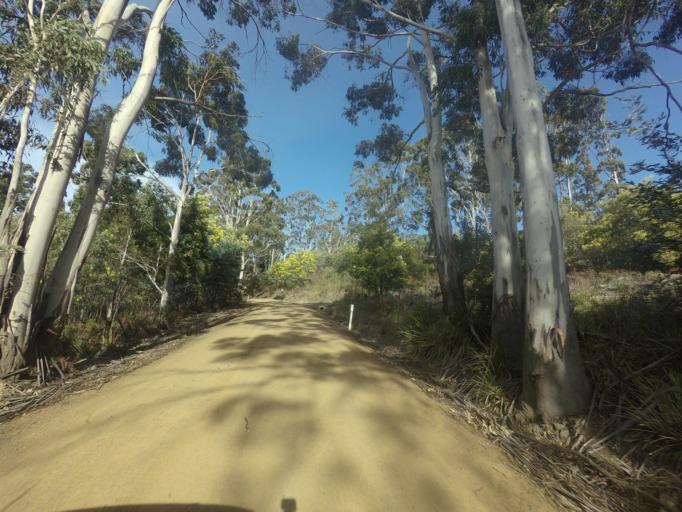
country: AU
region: Tasmania
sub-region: Kingborough
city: Kettering
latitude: -43.0900
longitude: 147.2657
